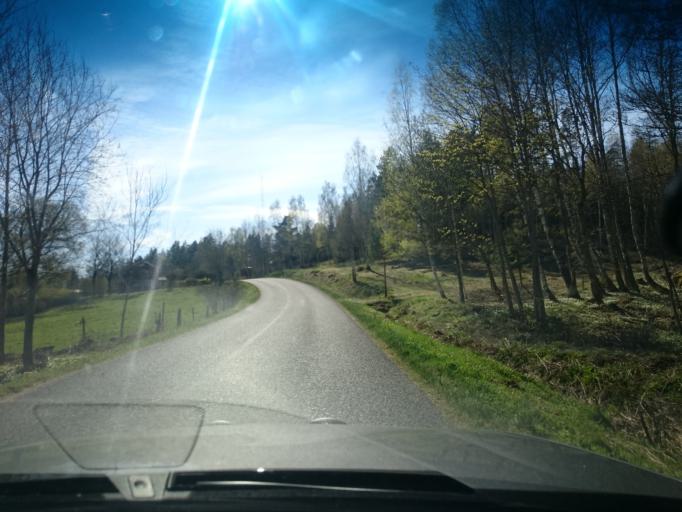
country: SE
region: Kalmar
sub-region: Hultsfreds Kommun
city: Virserum
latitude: 57.3300
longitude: 15.4893
